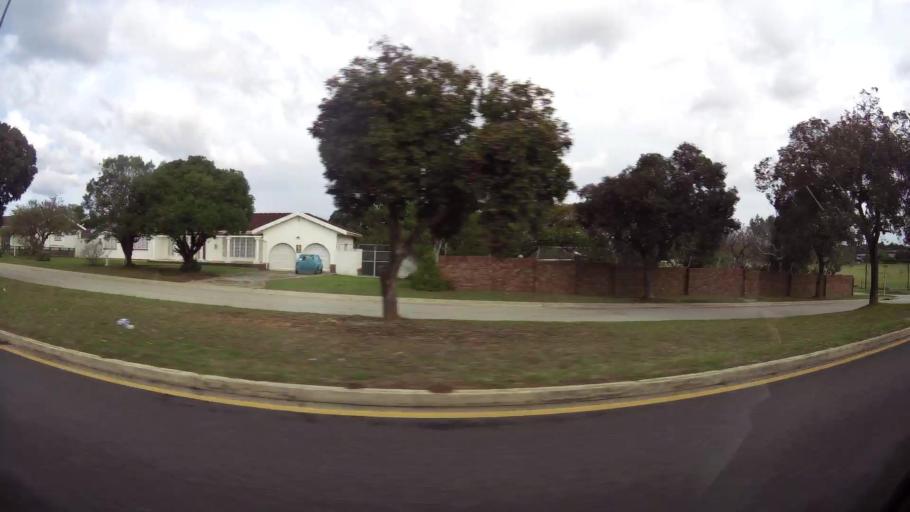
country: ZA
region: Eastern Cape
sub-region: Nelson Mandela Bay Metropolitan Municipality
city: Port Elizabeth
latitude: -33.9456
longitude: 25.5404
